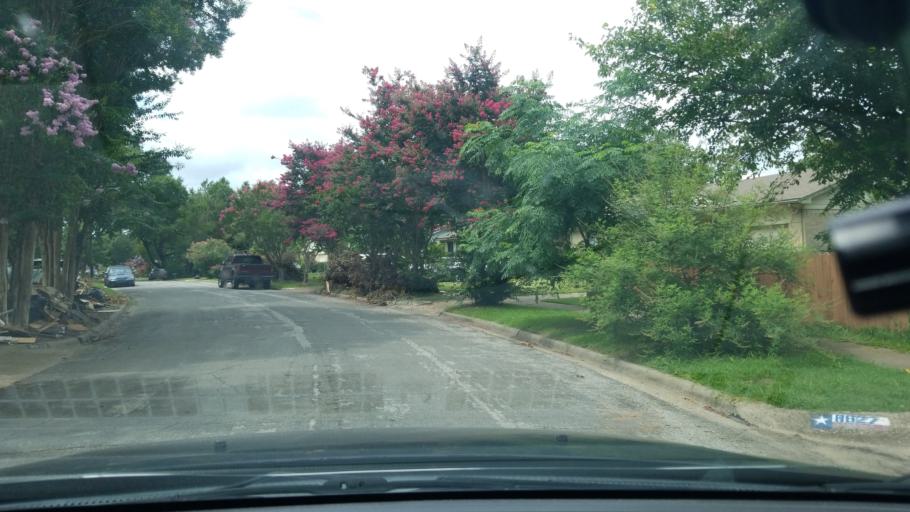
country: US
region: Texas
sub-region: Dallas County
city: Mesquite
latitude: 32.8140
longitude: -96.6780
